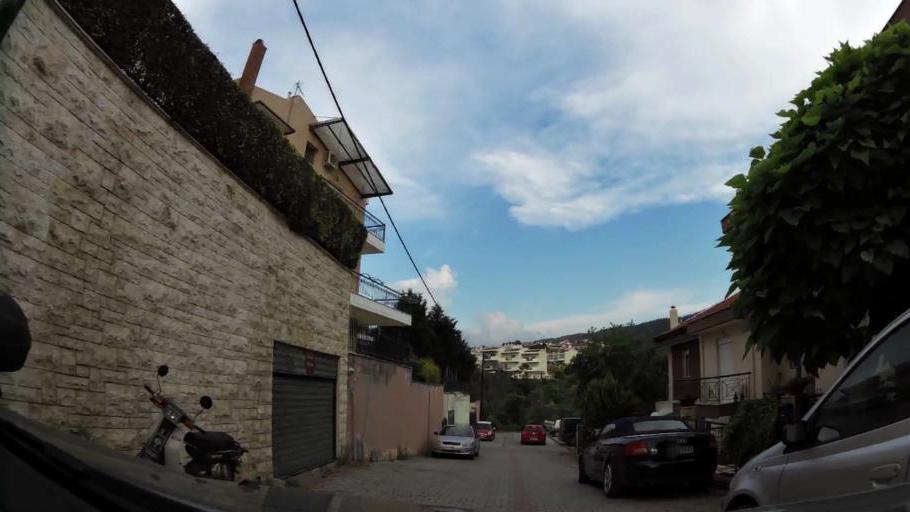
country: GR
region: Central Macedonia
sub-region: Nomos Thessalonikis
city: Pefka
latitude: 40.6619
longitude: 22.9766
